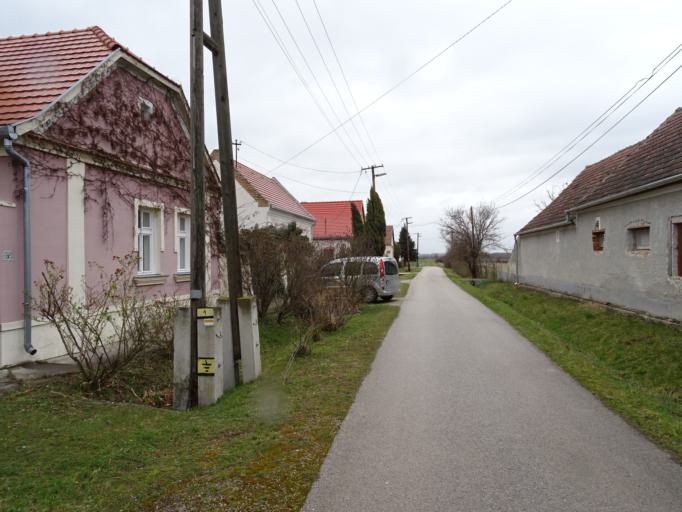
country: AT
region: Burgenland
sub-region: Politischer Bezirk Oberpullendorf
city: Nikitsch
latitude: 47.4911
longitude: 16.7015
